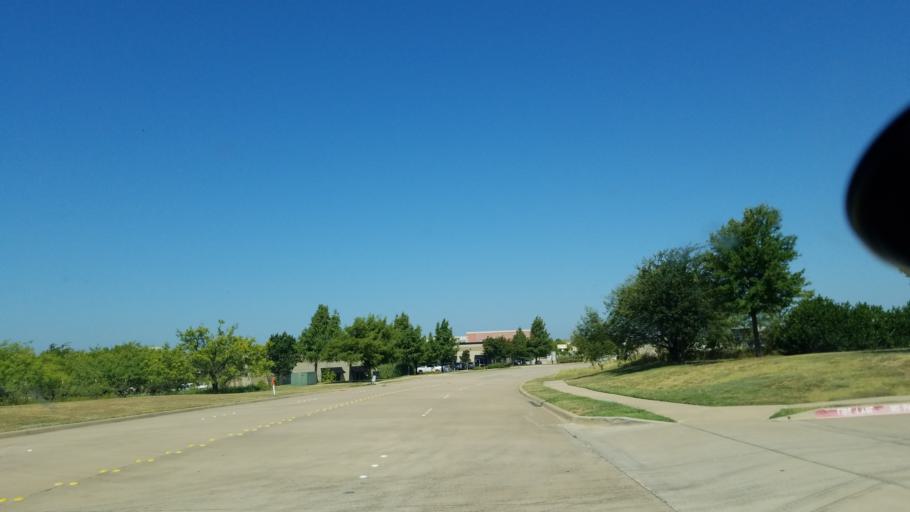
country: US
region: Texas
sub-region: Tarrant County
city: Mansfield
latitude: 32.5619
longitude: -97.1050
